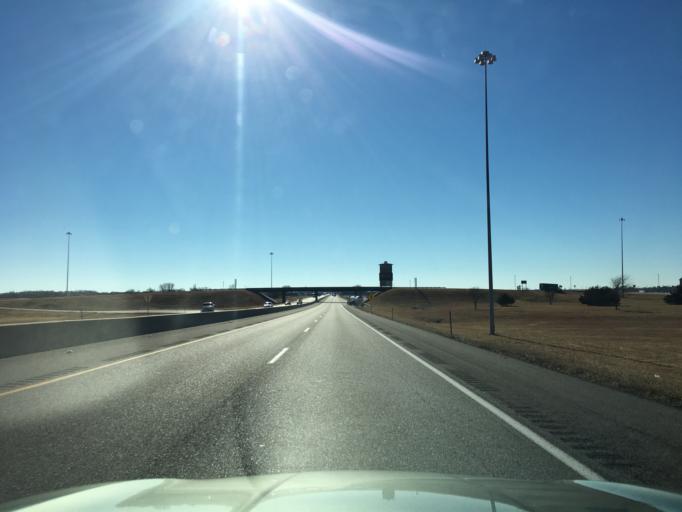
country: US
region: Kansas
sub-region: Sumner County
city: Mulvane
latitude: 37.4746
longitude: -97.3230
